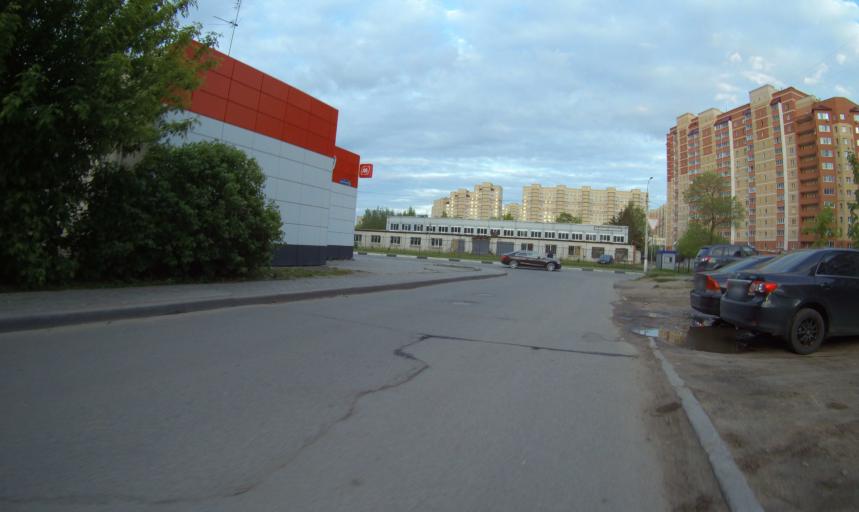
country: RU
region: Moskovskaya
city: Ramenskoye
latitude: 55.5762
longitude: 38.2472
